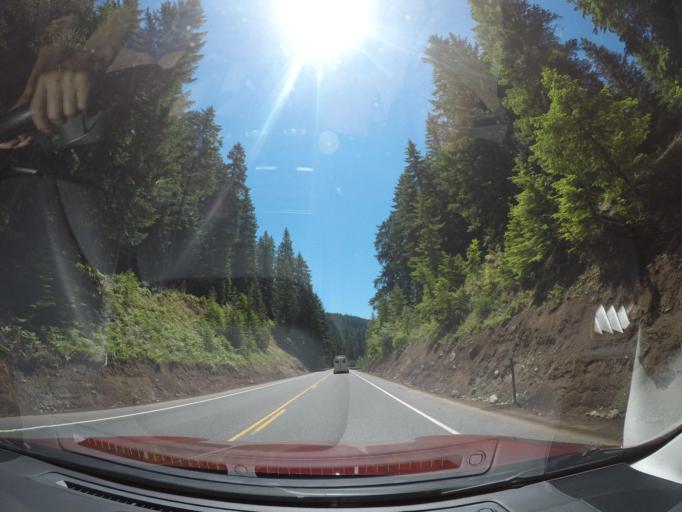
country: US
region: Oregon
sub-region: Linn County
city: Mill City
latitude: 44.5578
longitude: -121.9970
